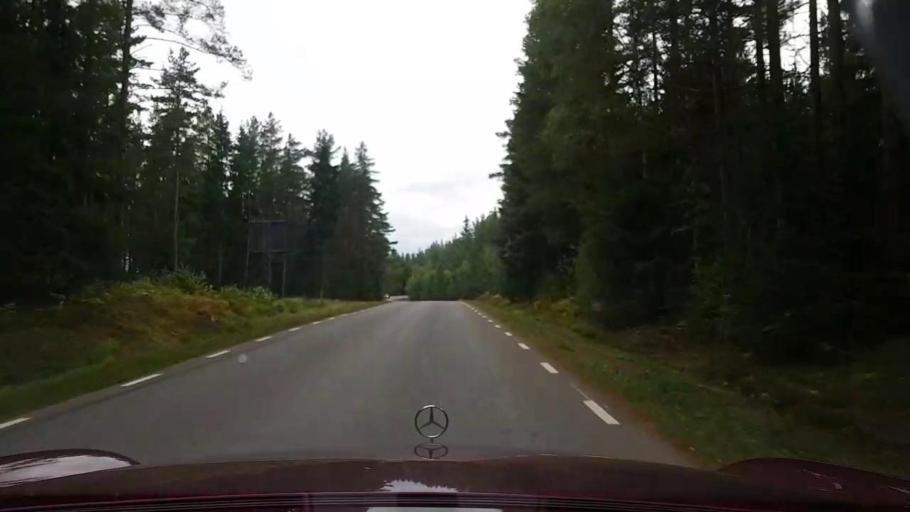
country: SE
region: Vaestra Goetaland
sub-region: Karlsborgs Kommun
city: Karlsborg
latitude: 58.7152
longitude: 14.5033
